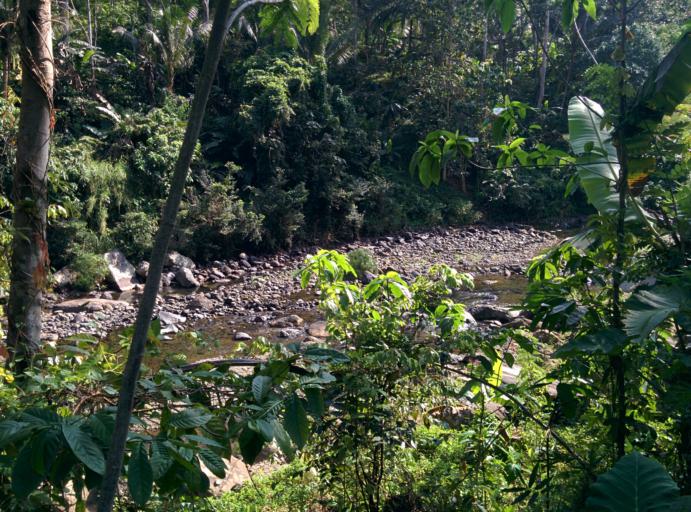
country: ID
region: East Java
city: Kedungbanteng Krajan
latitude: -8.3460
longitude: 112.7193
